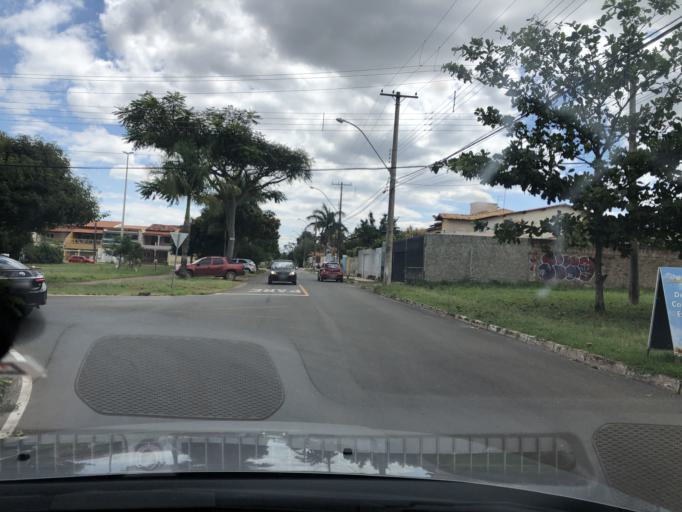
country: BR
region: Federal District
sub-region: Brasilia
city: Brasilia
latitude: -15.9937
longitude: -47.9946
